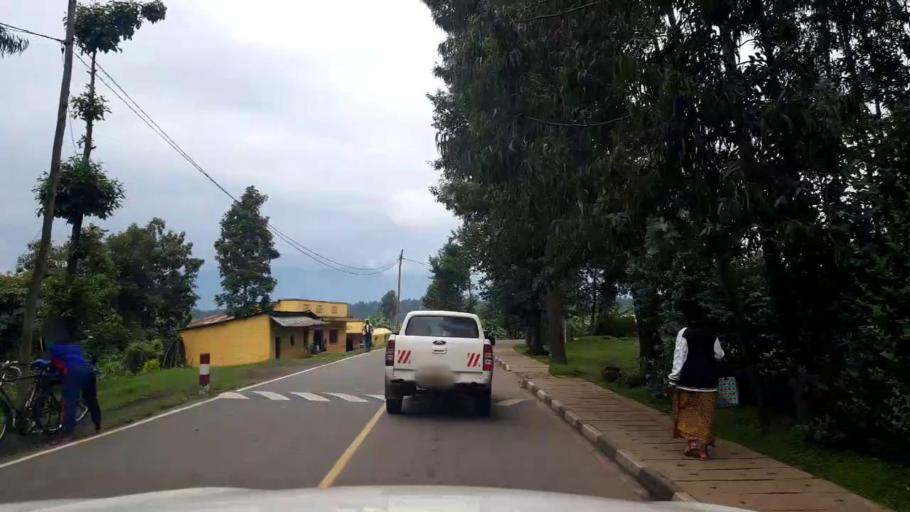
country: RW
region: Northern Province
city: Musanze
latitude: -1.4653
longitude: 29.6160
